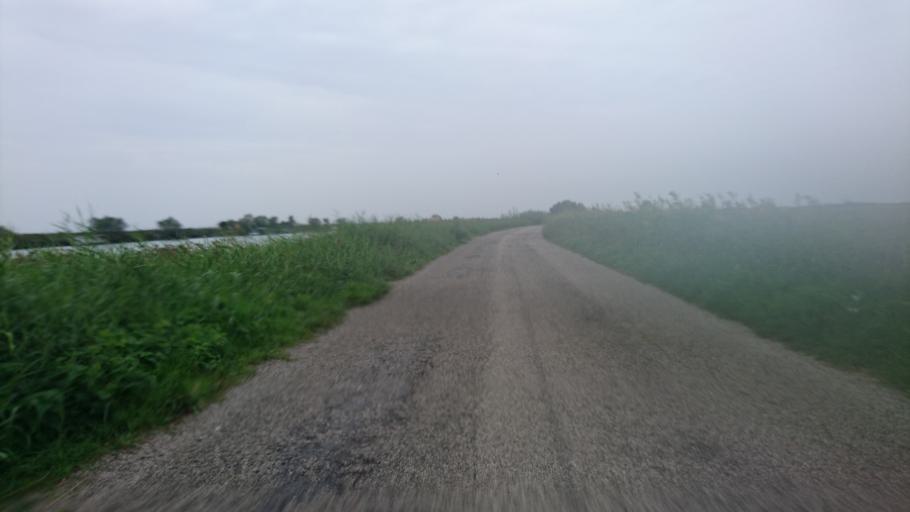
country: IT
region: Veneto
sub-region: Provincia di Rovigo
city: Scardovari
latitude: 44.8177
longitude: 12.3930
